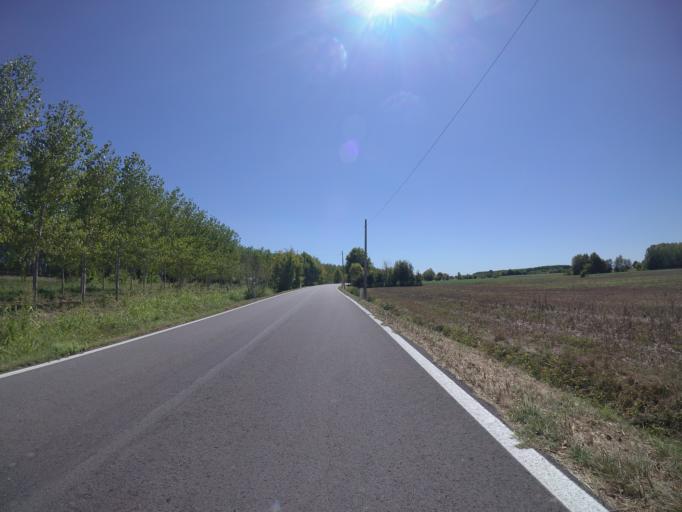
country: IT
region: Friuli Venezia Giulia
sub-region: Provincia di Udine
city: Rivignano
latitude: 45.8632
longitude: 13.0280
